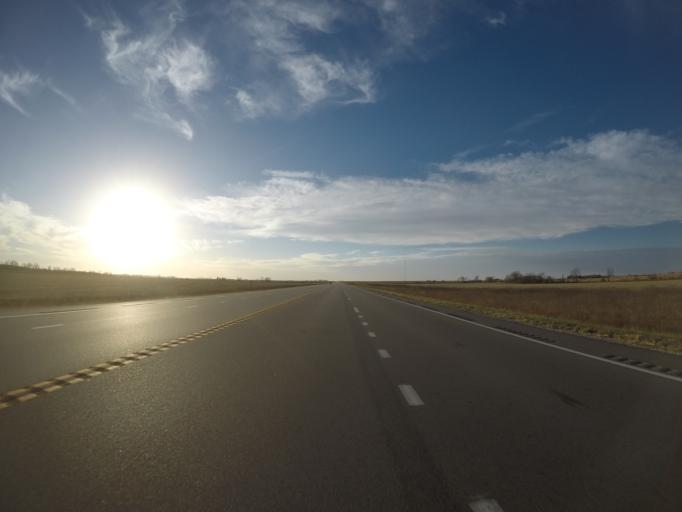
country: US
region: Kansas
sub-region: Chase County
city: Cottonwood Falls
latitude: 38.4048
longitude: -96.3972
